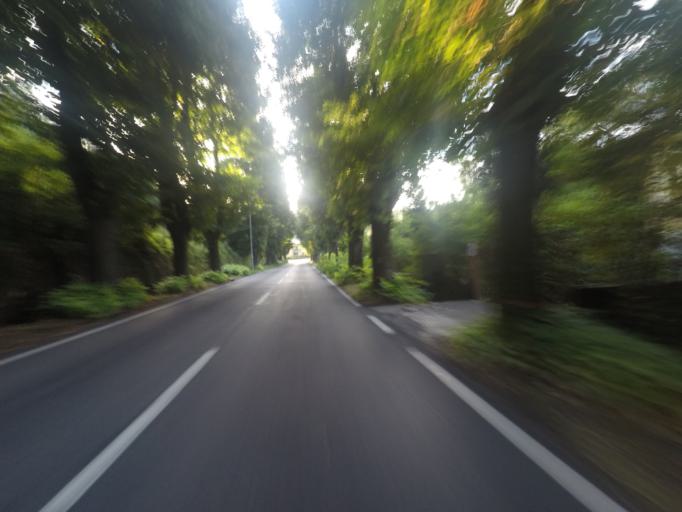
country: IT
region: Tuscany
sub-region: Provincia di Lucca
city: Stiava
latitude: 43.9211
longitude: 10.3321
